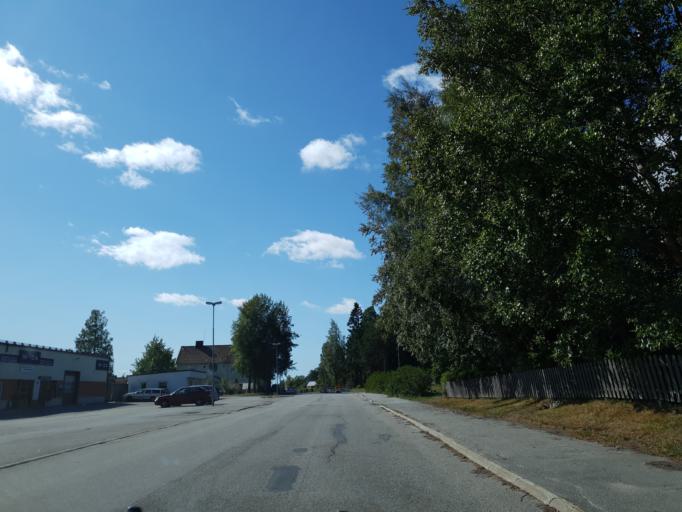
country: SE
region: Vaesterbotten
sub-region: Umea Kommun
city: Holmsund
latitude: 63.7104
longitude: 20.3712
